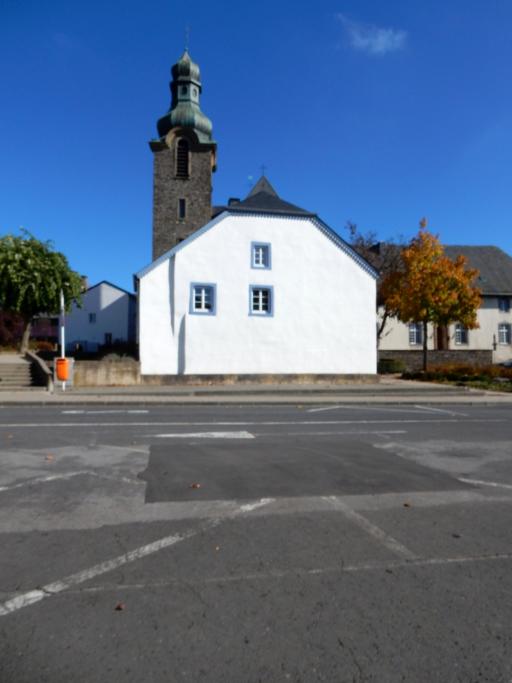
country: LU
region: Diekirch
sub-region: Canton de Clervaux
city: Troisvierges
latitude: 50.1206
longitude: 6.0014
